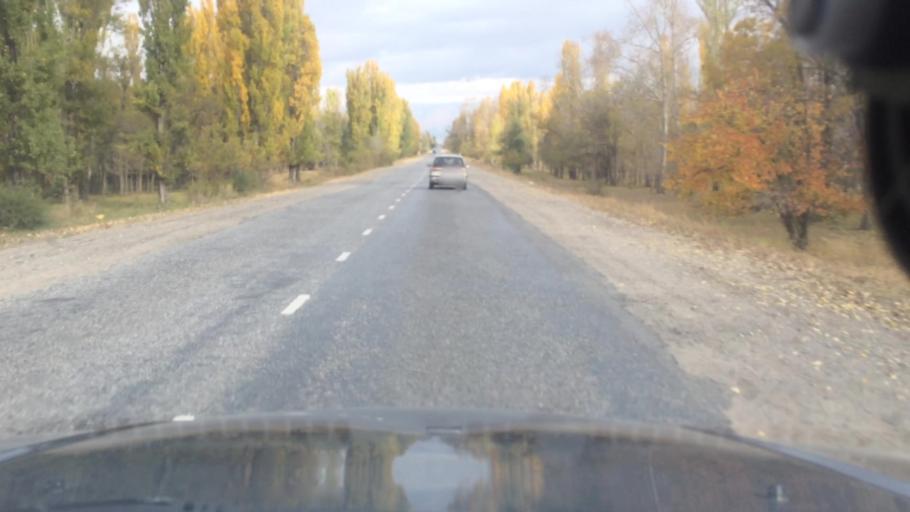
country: KG
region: Ysyk-Koel
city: Tyup
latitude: 42.6123
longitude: 78.3666
